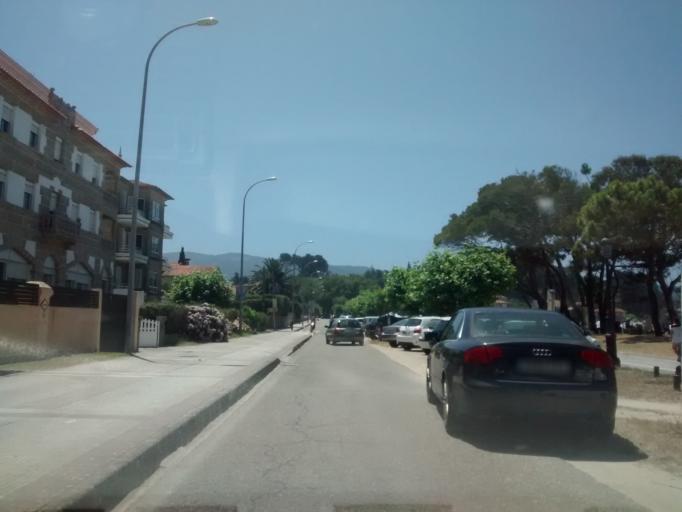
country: ES
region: Galicia
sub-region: Provincia de Pontevedra
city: Nigran
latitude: 42.1273
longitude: -8.8195
